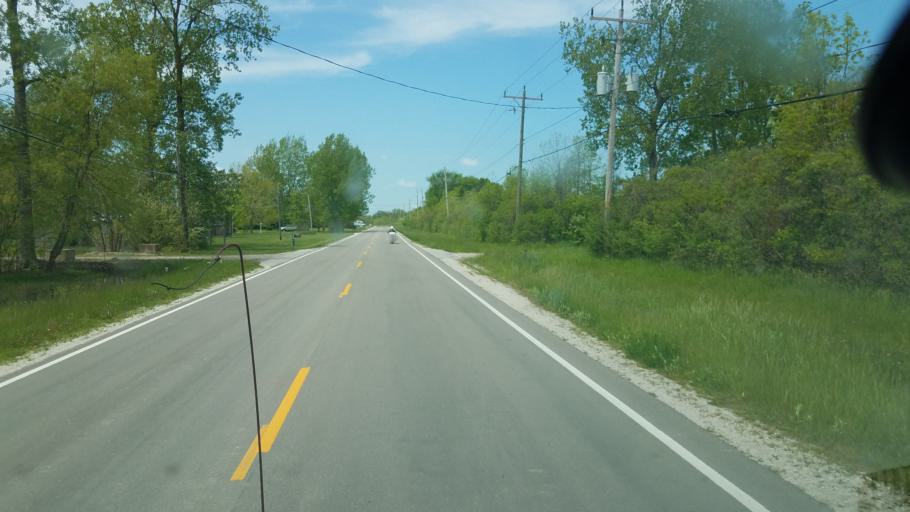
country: US
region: Ohio
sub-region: Ottawa County
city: Port Clinton
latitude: 41.5228
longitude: -83.0010
